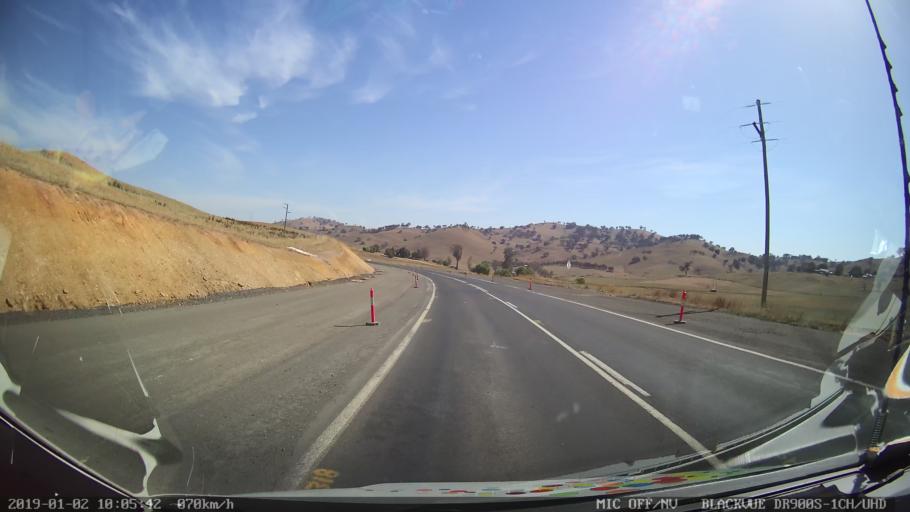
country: AU
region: New South Wales
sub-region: Gundagai
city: Gundagai
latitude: -35.1565
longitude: 148.1181
